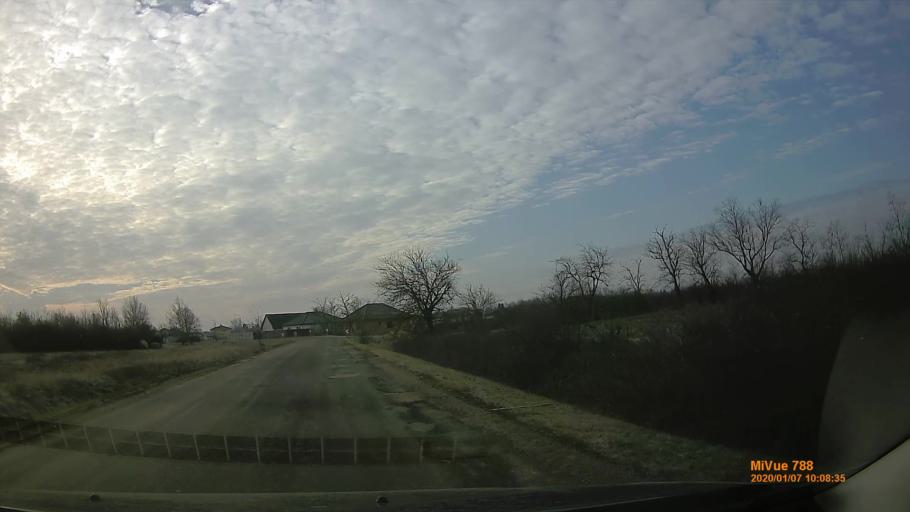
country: HU
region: Gyor-Moson-Sopron
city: Rajka
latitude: 47.9220
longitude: 17.1554
